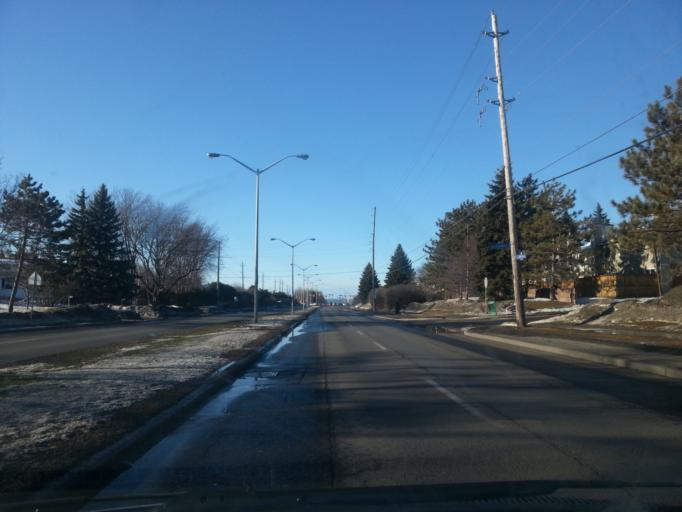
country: CA
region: Quebec
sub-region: Outaouais
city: Gatineau
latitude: 45.4744
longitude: -75.4958
